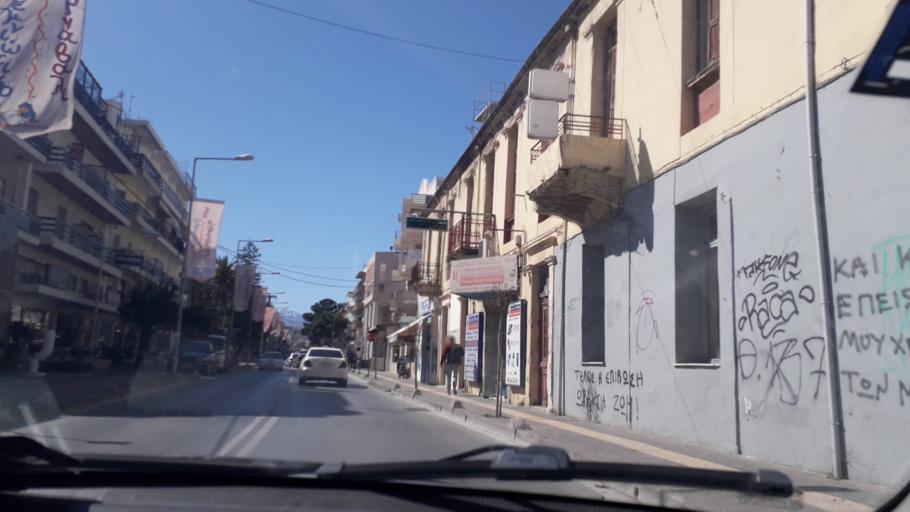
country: GR
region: Crete
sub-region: Nomos Rethymnis
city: Rethymno
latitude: 35.3673
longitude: 24.4723
